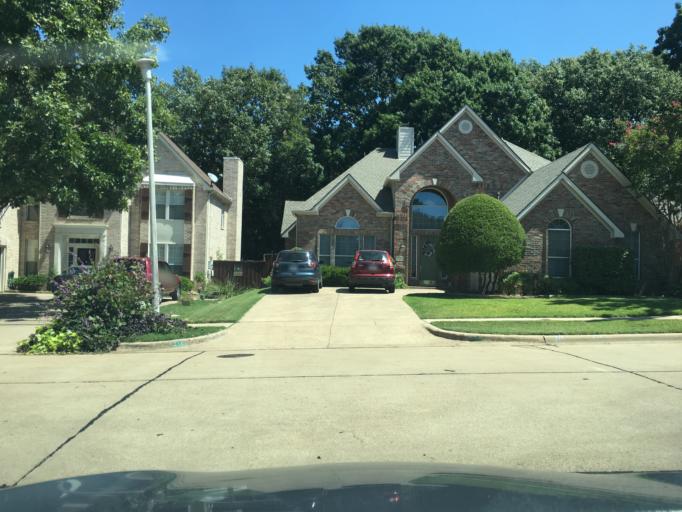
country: US
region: Texas
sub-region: Dallas County
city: Sachse
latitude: 32.9684
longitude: -96.6324
